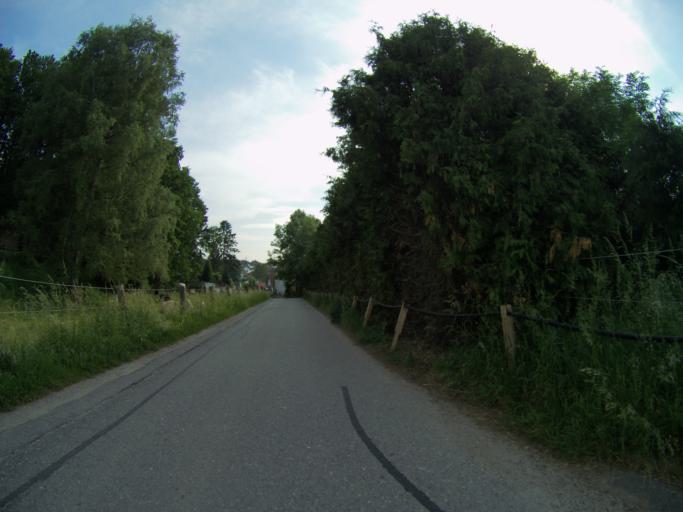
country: DE
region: Bavaria
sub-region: Upper Bavaria
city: Marzling
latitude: 48.4218
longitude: 11.7748
